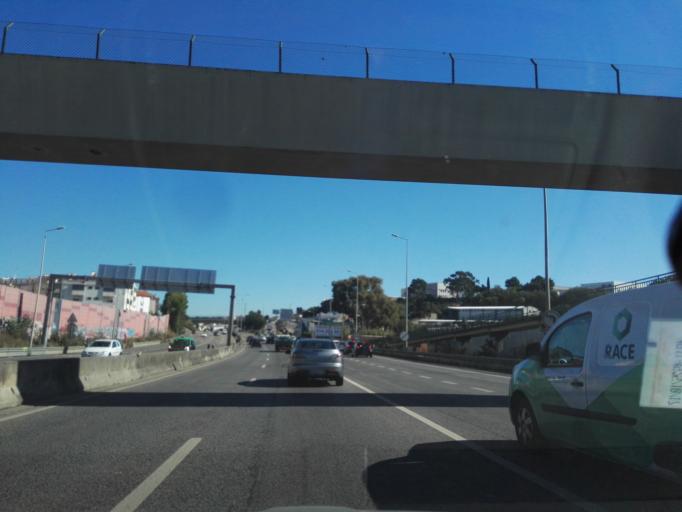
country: PT
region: Lisbon
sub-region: Sintra
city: Cacem
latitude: 38.7660
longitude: -9.3105
